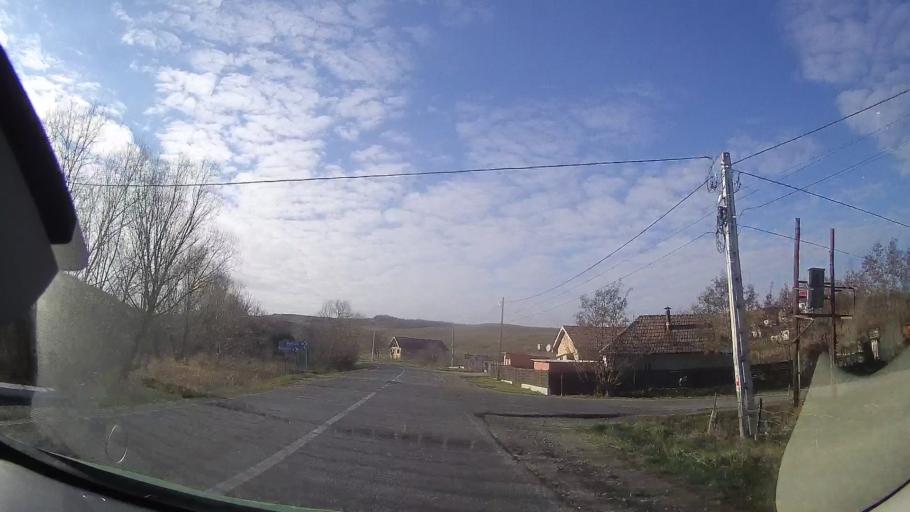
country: RO
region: Cluj
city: Caianu Mic
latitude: 46.8122
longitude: 23.8598
